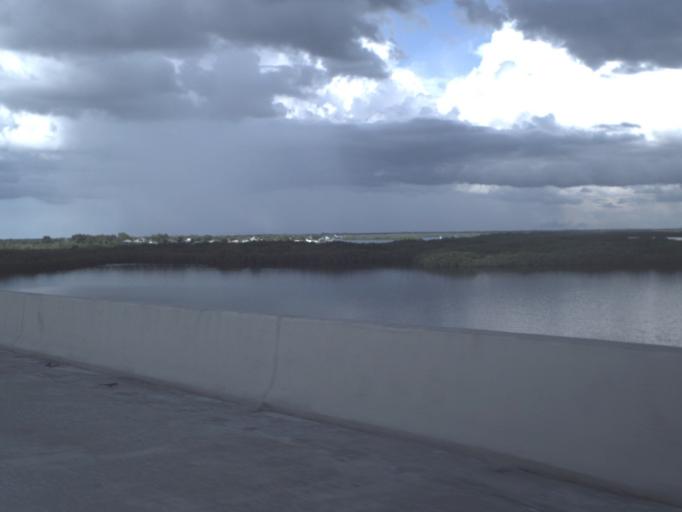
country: US
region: Florida
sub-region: Charlotte County
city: Harbour Heights
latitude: 26.9605
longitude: -82.0200
